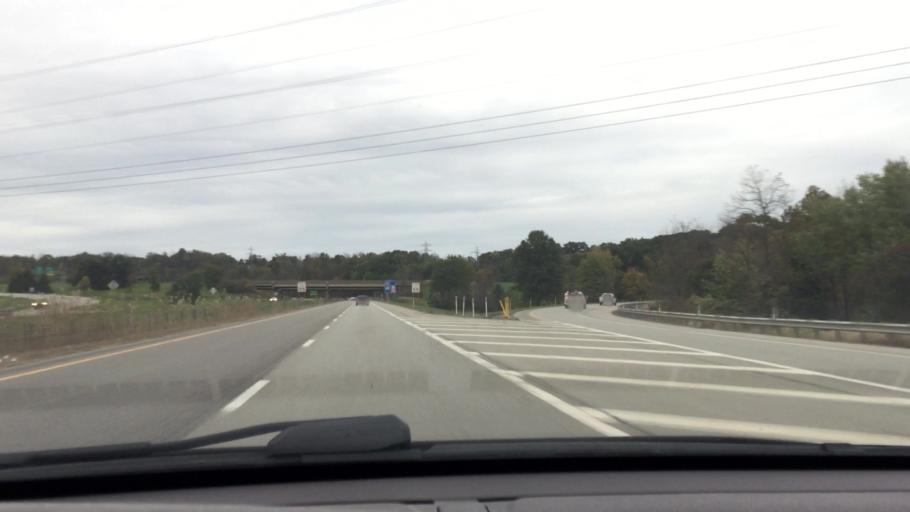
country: US
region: Pennsylvania
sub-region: Lawrence County
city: Oakland
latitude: 40.9886
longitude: -80.3913
